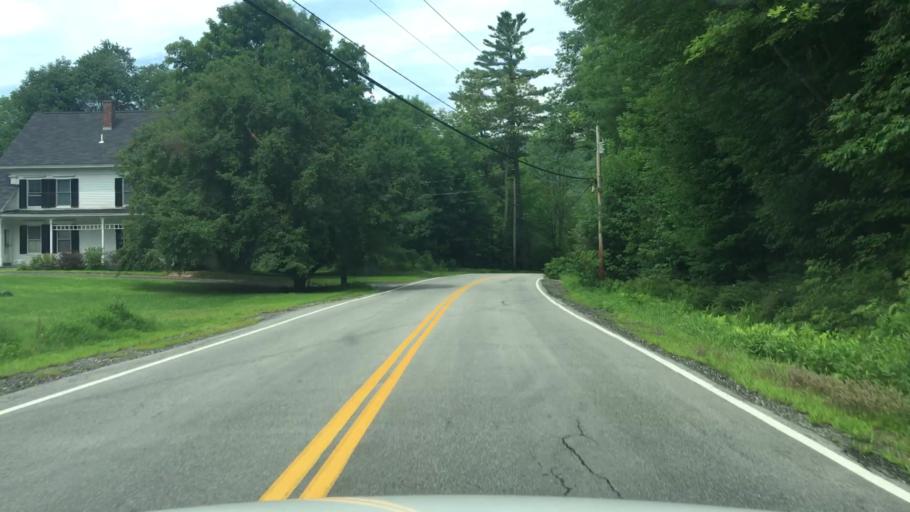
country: US
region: New Hampshire
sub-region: Grafton County
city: Rumney
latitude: 43.8035
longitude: -71.8071
